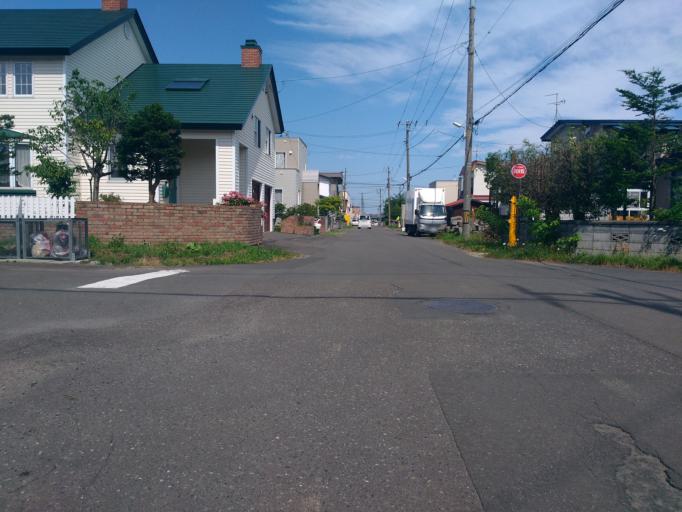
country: JP
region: Hokkaido
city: Ebetsu
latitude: 43.0806
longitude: 141.5087
